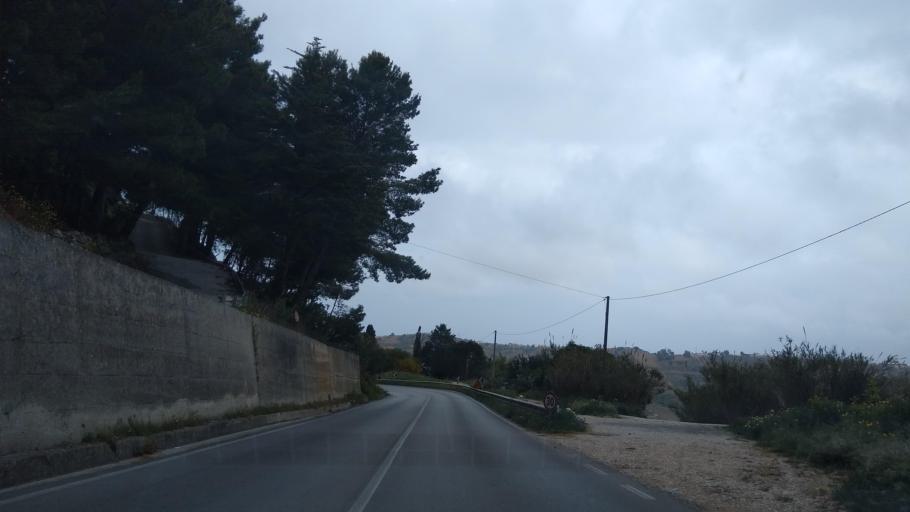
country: IT
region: Sicily
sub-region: Trapani
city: Alcamo
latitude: 37.9777
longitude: 12.9387
